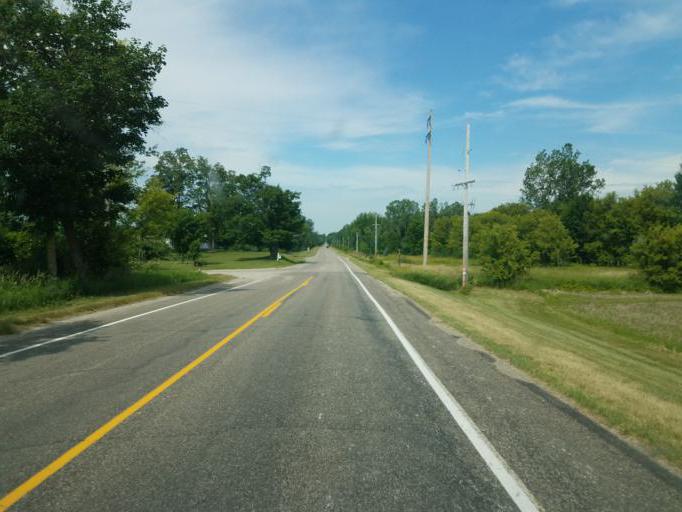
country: US
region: Michigan
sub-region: Eaton County
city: Charlotte
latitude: 42.6264
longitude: -84.9553
